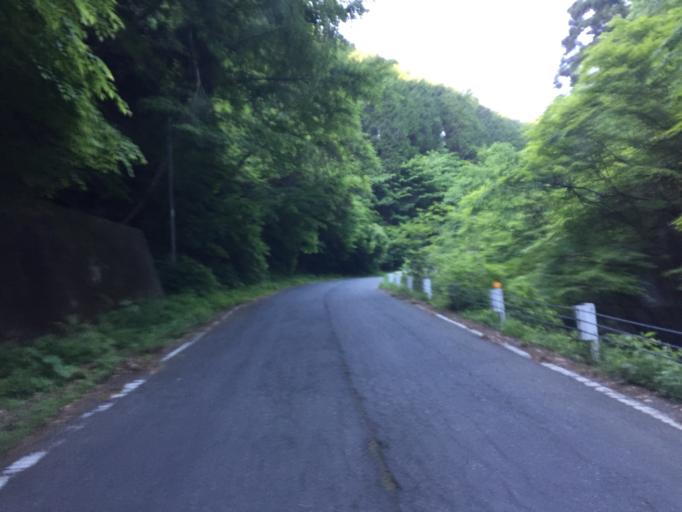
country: JP
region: Ibaraki
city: Kitaibaraki
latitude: 36.8830
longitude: 140.6278
